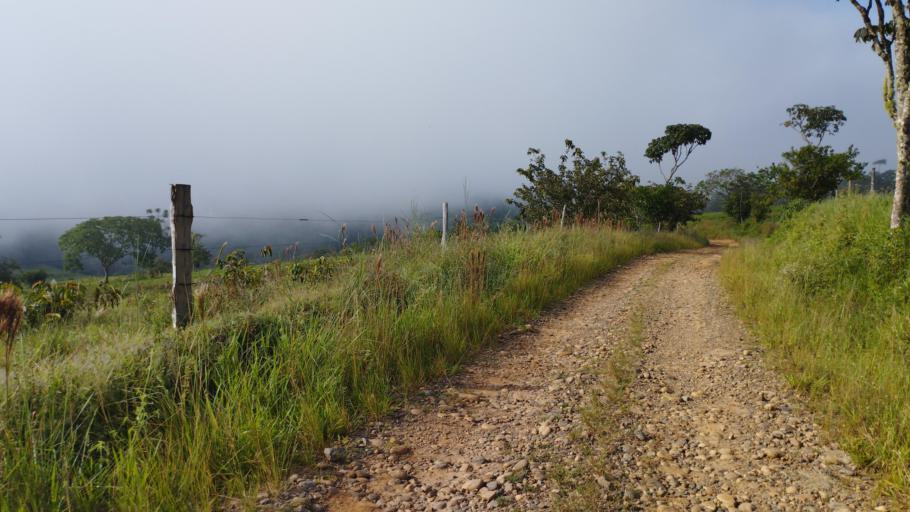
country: CO
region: Casanare
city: Sabanalarga
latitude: 4.7675
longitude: -73.0800
